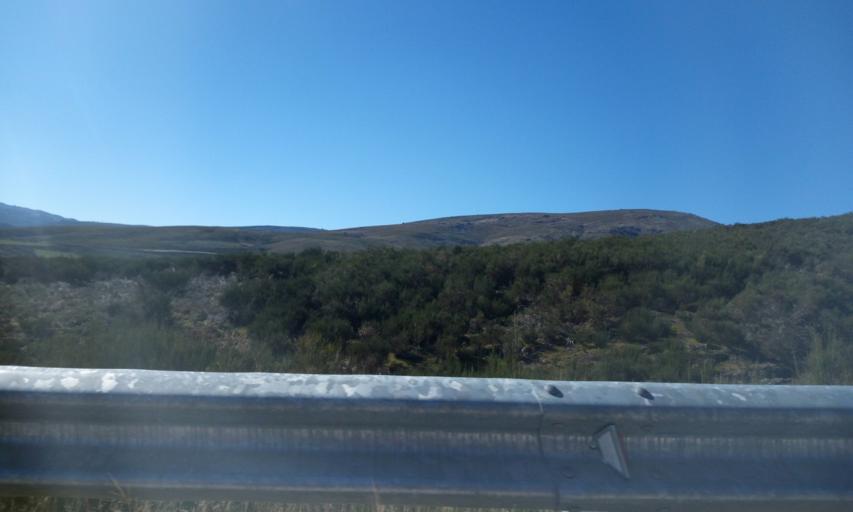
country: PT
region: Guarda
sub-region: Manteigas
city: Manteigas
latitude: 40.4628
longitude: -7.4992
